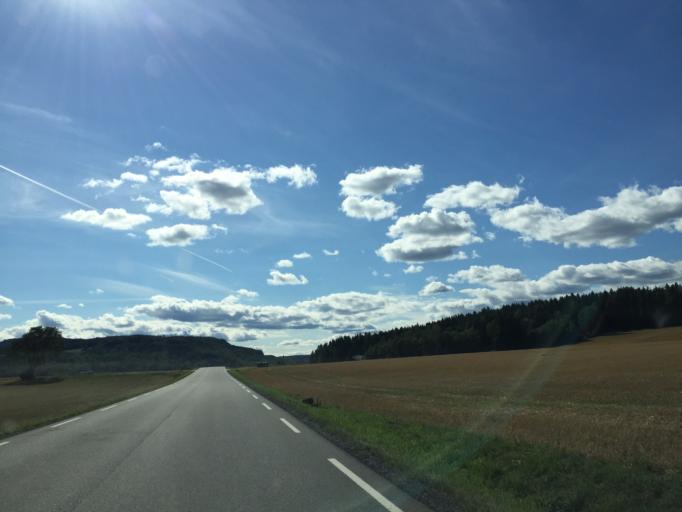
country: NO
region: Buskerud
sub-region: Ovre Eiker
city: Hokksund
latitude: 59.7058
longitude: 9.8588
